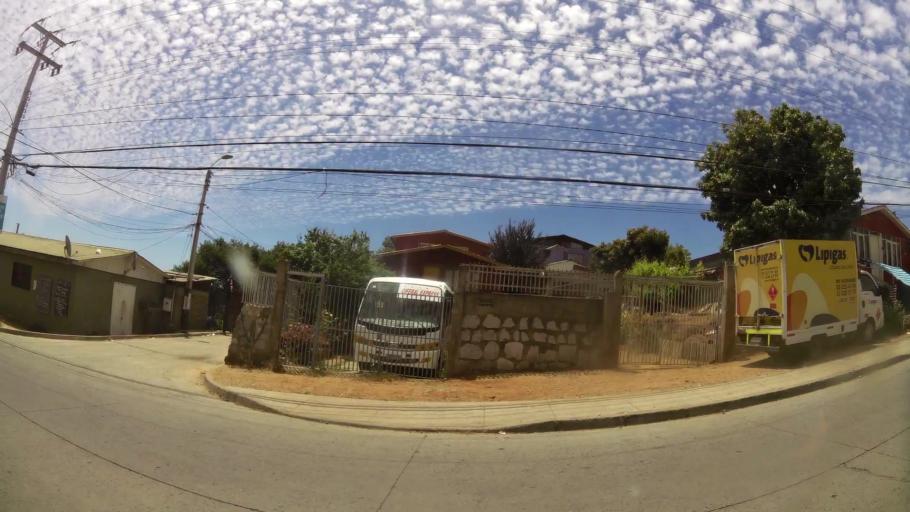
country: CL
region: Valparaiso
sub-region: Provincia de Valparaiso
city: Vina del Mar
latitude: -33.0524
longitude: -71.5687
